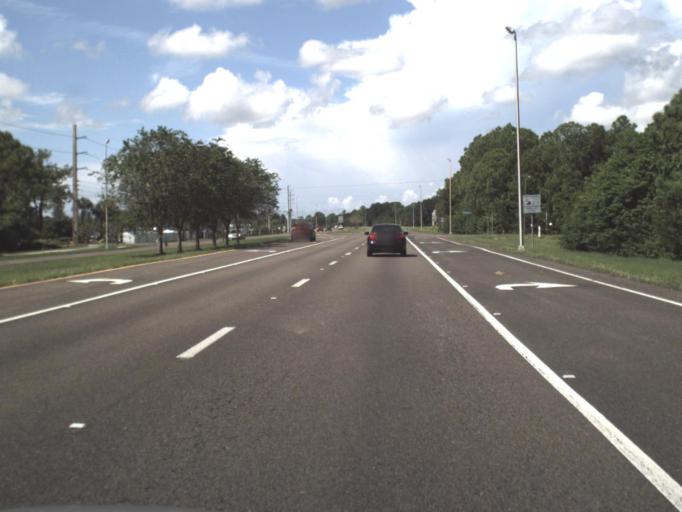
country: US
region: Florida
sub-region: Sarasota County
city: Warm Mineral Springs
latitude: 27.0484
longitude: -82.2802
